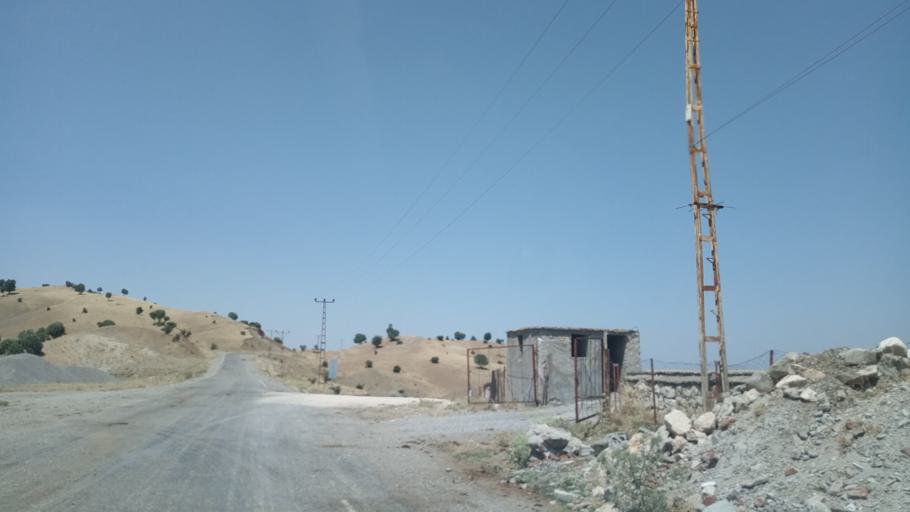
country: TR
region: Siirt
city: Dilektepe
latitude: 38.0765
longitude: 41.8224
